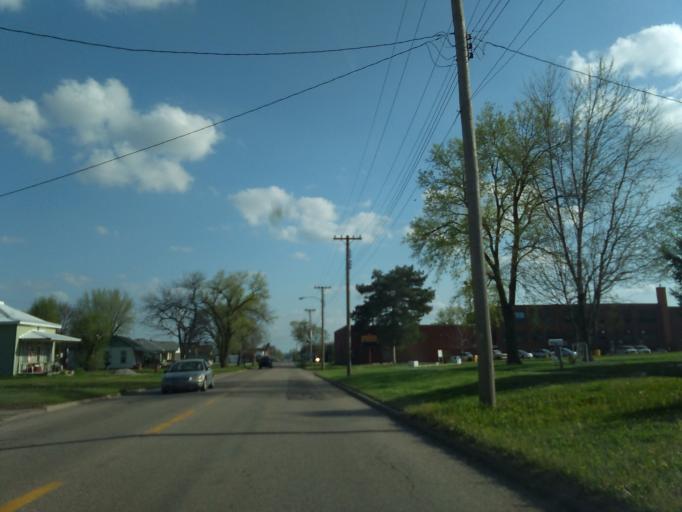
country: US
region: Nebraska
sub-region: Webster County
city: Red Cloud
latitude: 40.0937
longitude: -98.5194
